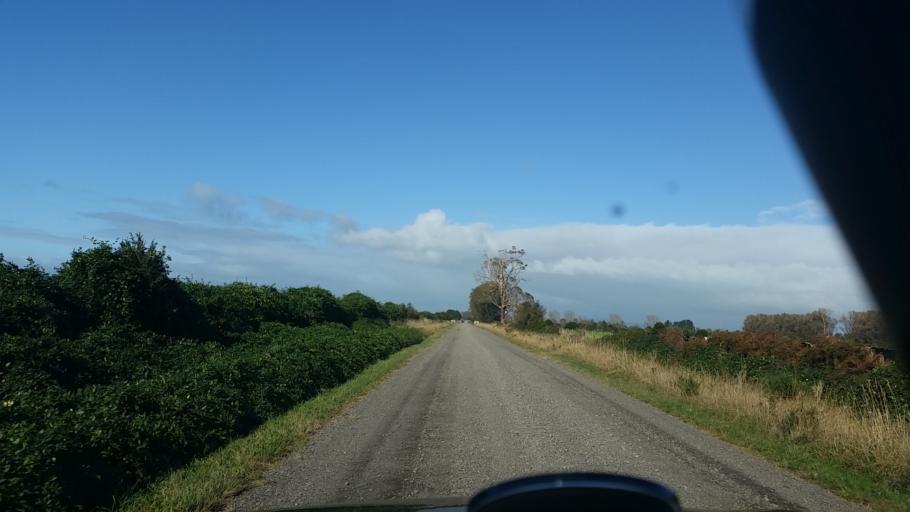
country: NZ
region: Bay of Plenty
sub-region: Western Bay of Plenty District
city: Katikati
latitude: -37.5856
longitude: 175.7131
